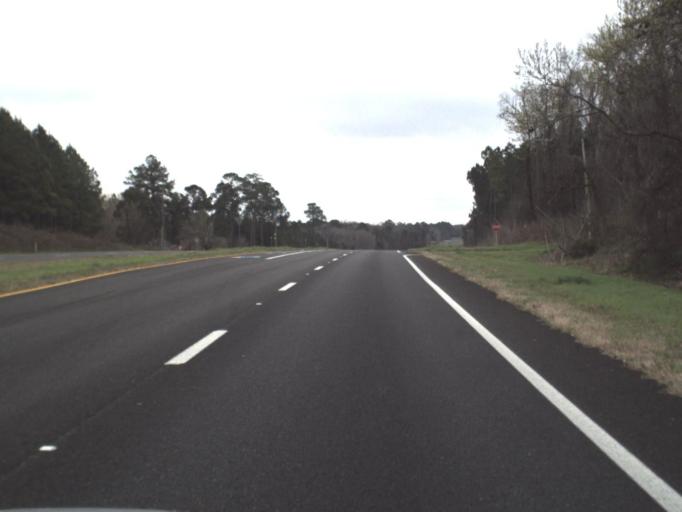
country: US
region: Florida
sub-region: Jefferson County
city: Monticello
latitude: 30.3855
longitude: -83.8326
